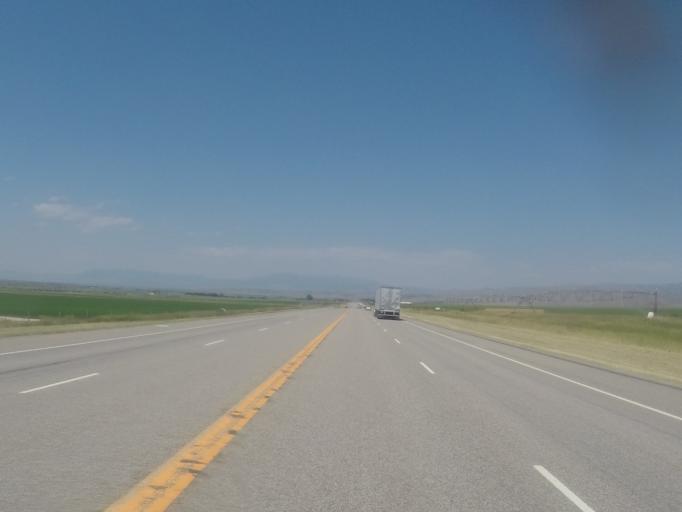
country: US
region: Montana
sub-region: Broadwater County
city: Townsend
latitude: 46.1169
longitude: -111.5012
